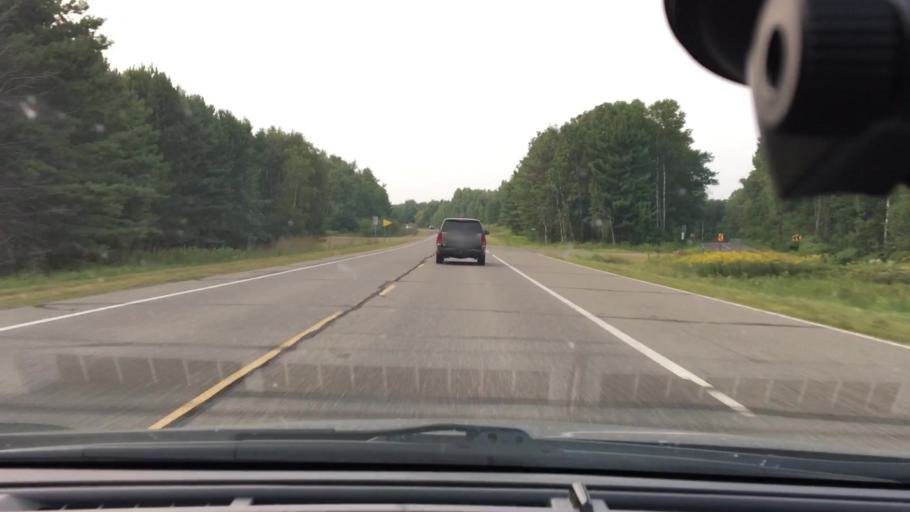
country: US
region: Minnesota
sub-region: Crow Wing County
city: Crosby
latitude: 46.4321
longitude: -93.8736
